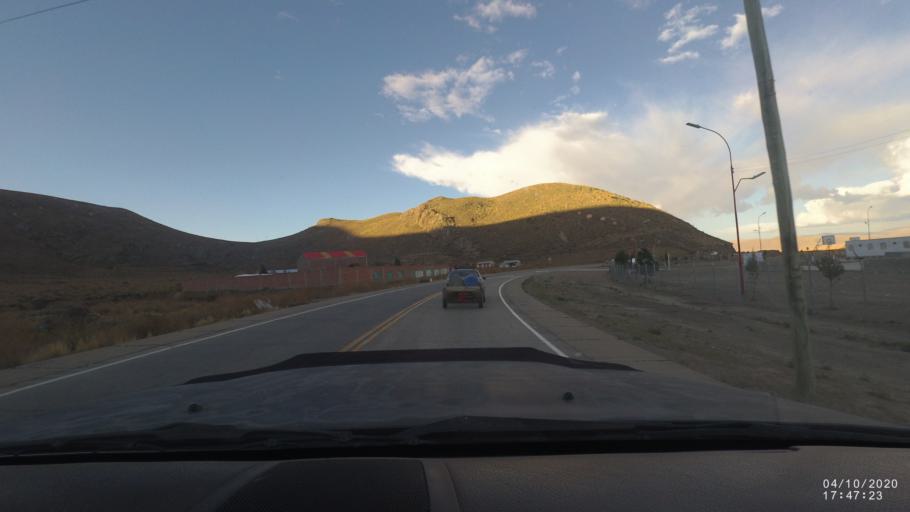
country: BO
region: Oruro
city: Oruro
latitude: -18.0235
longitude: -67.1443
